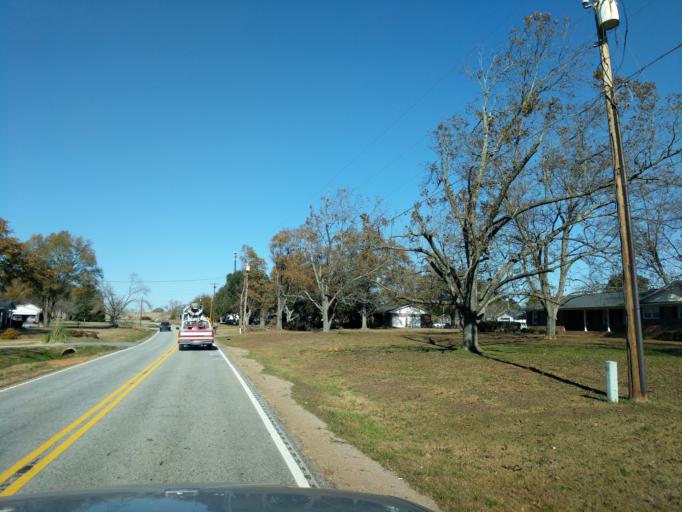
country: US
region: South Carolina
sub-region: Spartanburg County
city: Duncan
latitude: 35.0042
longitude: -82.1760
